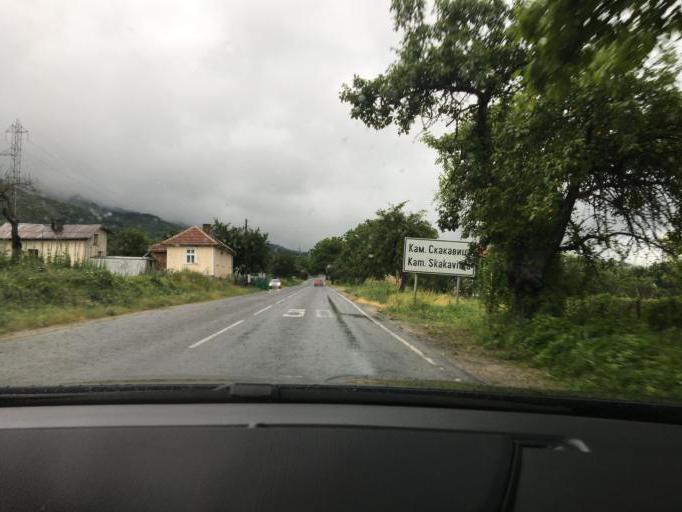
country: MK
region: Kriva Palanka
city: Kriva Palanka
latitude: 42.2383
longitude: 22.5085
